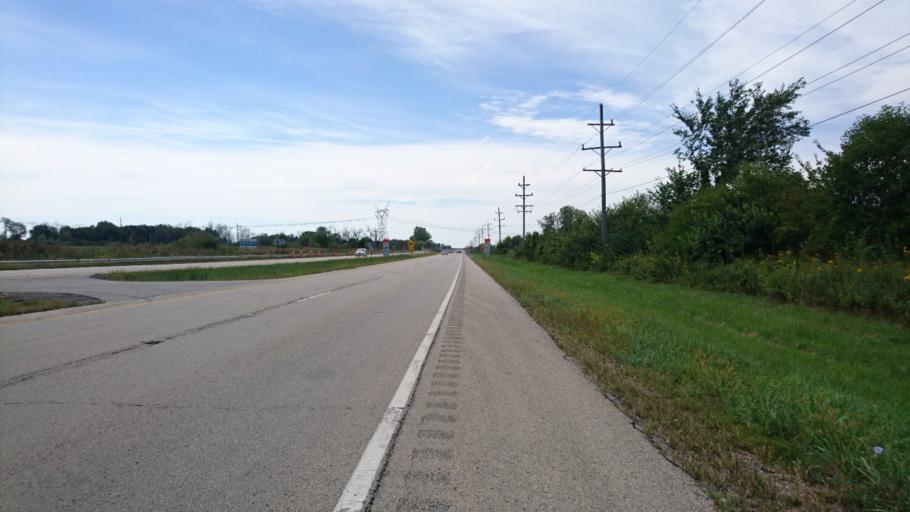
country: US
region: Illinois
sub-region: Will County
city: Elwood
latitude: 41.3960
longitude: -88.1143
